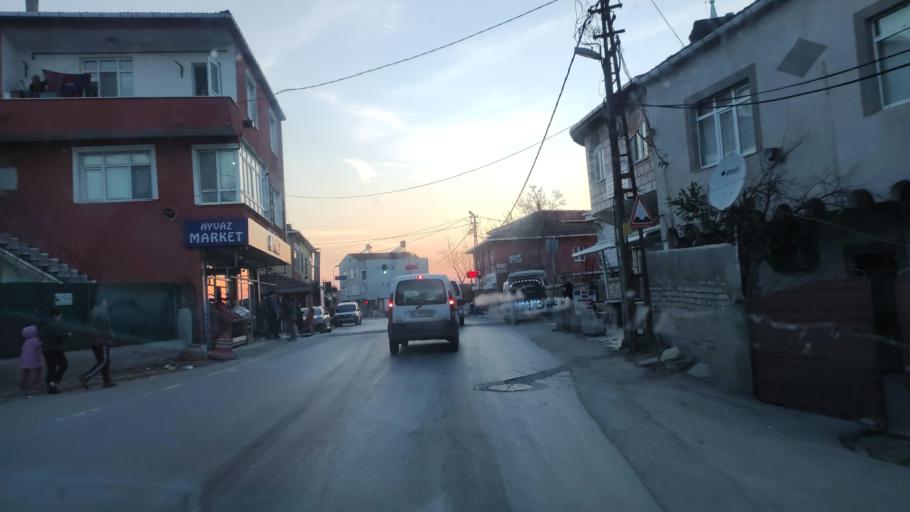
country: TR
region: Istanbul
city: Basaksehir
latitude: 41.1113
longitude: 28.7408
